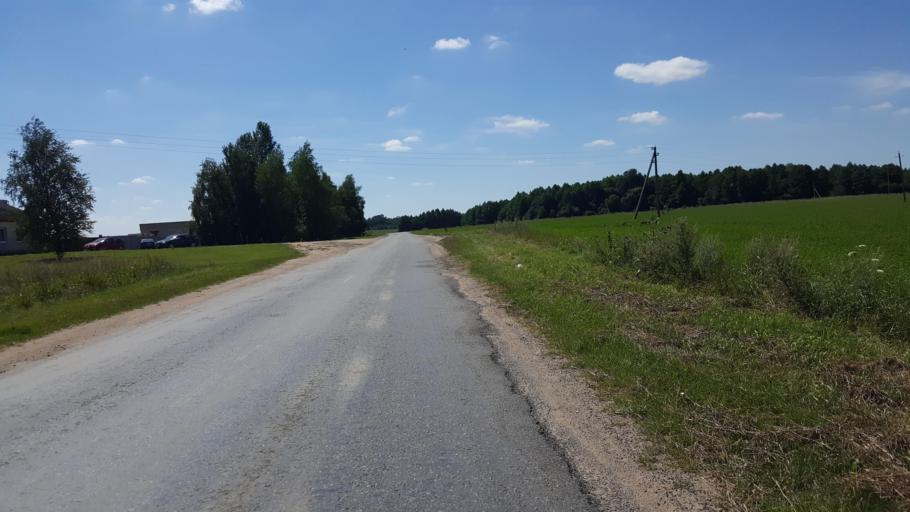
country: BY
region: Brest
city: Charnawchytsy
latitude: 52.3404
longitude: 23.6053
